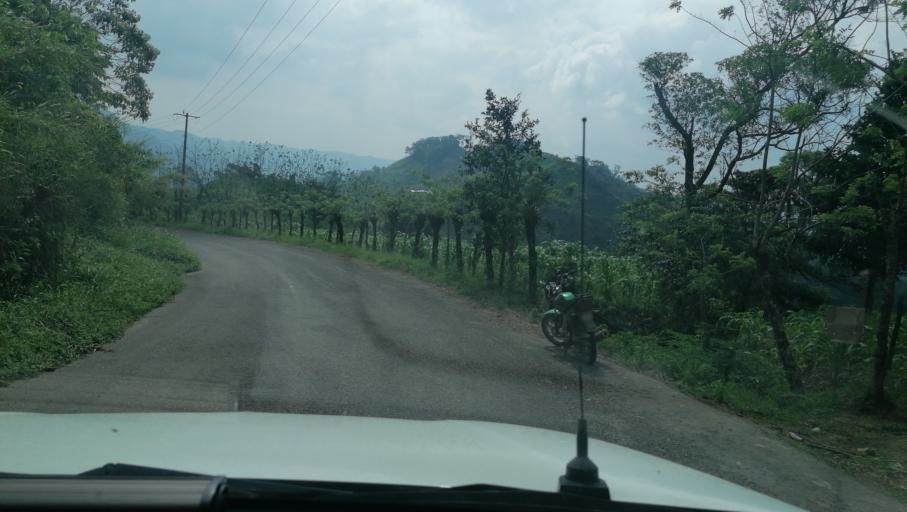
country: MX
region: Chiapas
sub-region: Francisco Leon
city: San Miguel la Sardina
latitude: 17.2370
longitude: -93.3246
